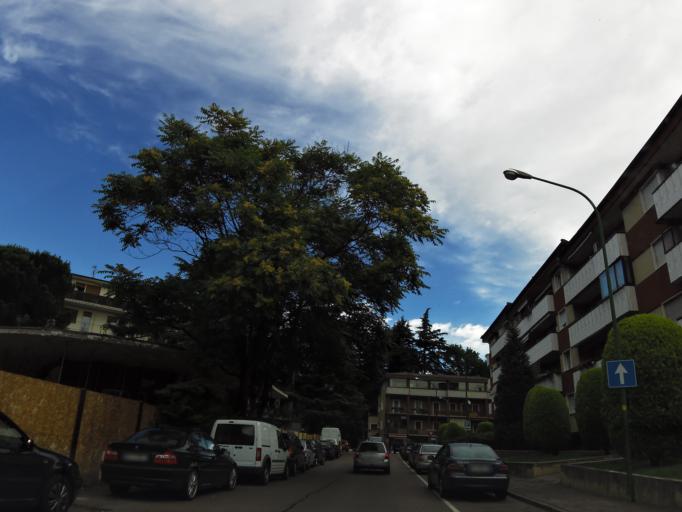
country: IT
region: Trentino-Alto Adige
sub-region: Bolzano
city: Merano
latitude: 46.6658
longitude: 11.1590
